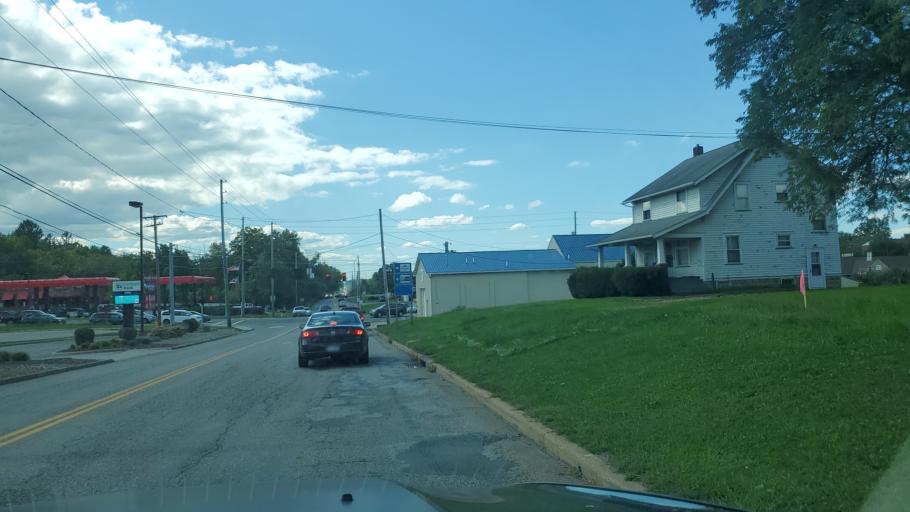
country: US
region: Ohio
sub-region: Mahoning County
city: Boardman
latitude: 40.9880
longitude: -80.6615
